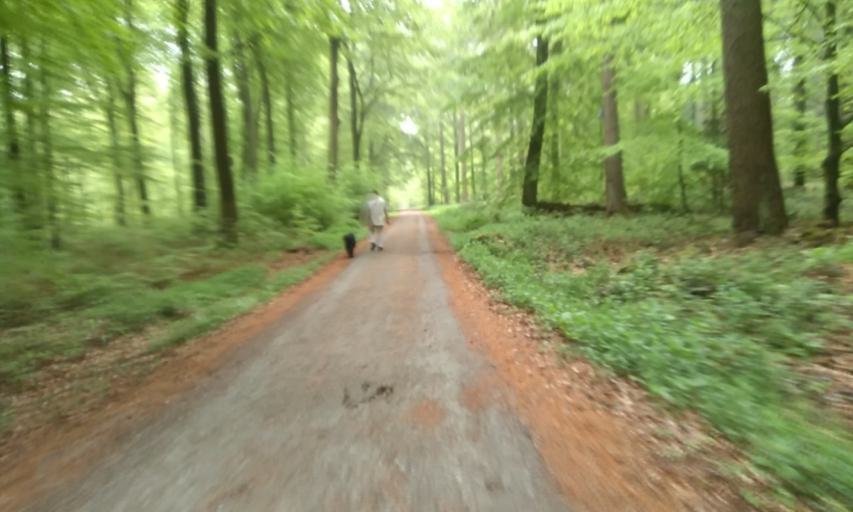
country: DE
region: Lower Saxony
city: Nottensdorf
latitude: 53.4722
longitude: 9.6363
